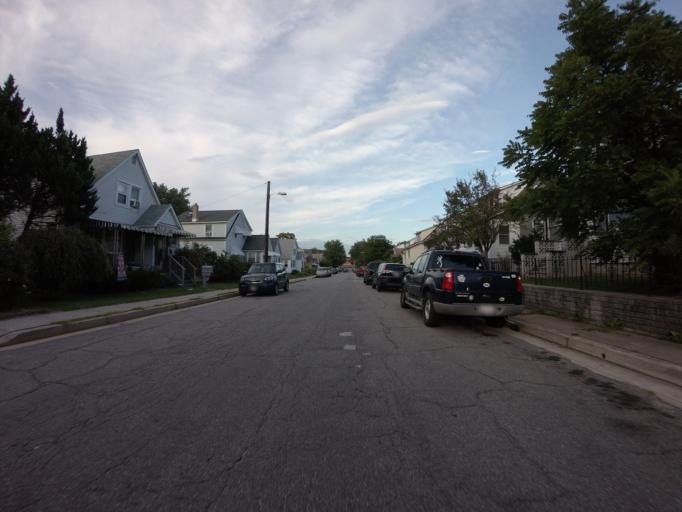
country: US
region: Maryland
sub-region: Baltimore County
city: Dundalk
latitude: 39.2624
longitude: -76.5293
